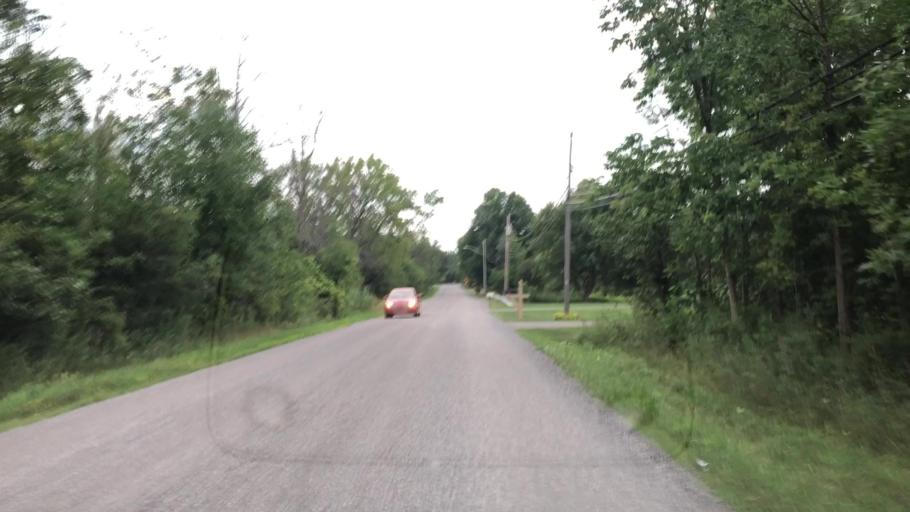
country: US
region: New York
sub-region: Erie County
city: Elma Center
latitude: 42.8398
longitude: -78.6798
